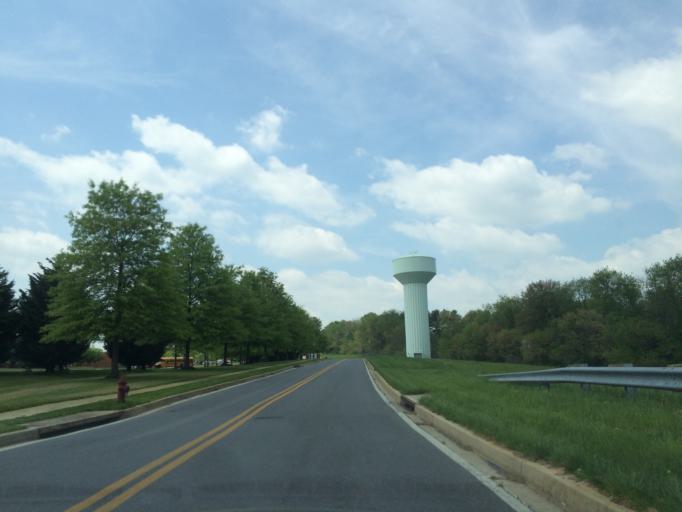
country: US
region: Maryland
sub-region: Carroll County
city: Eldersburg
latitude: 39.4249
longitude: -76.9888
